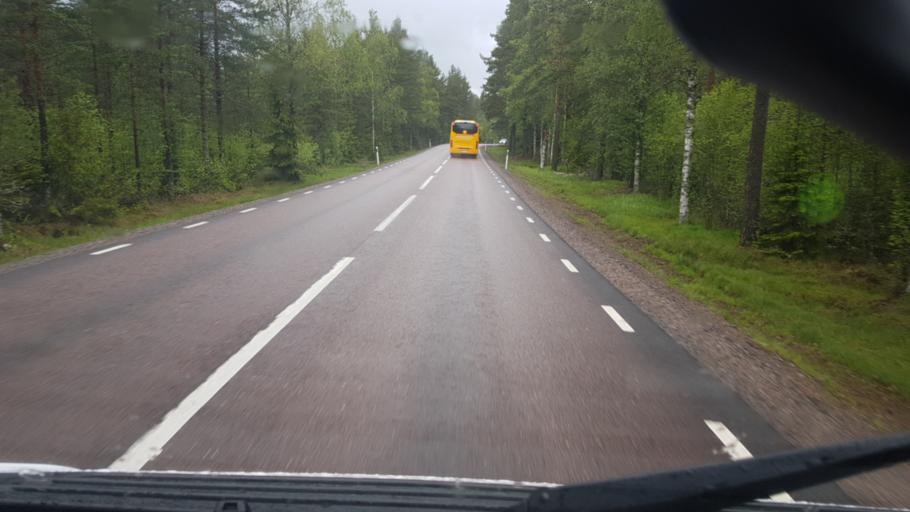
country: SE
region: Vaermland
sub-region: Eda Kommun
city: Charlottenberg
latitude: 59.8599
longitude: 12.2992
